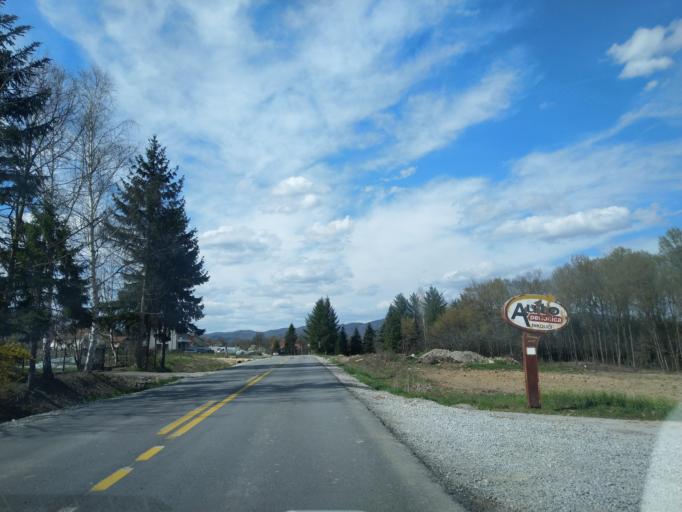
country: RS
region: Central Serbia
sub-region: Zlatiborski Okrug
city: Pozega
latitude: 43.8180
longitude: 20.0864
